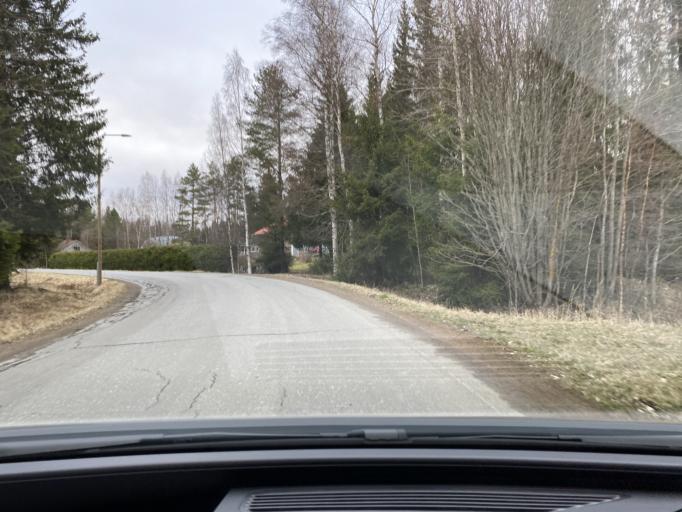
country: FI
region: Satakunta
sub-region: Pori
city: Huittinen
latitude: 61.1678
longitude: 22.7216
